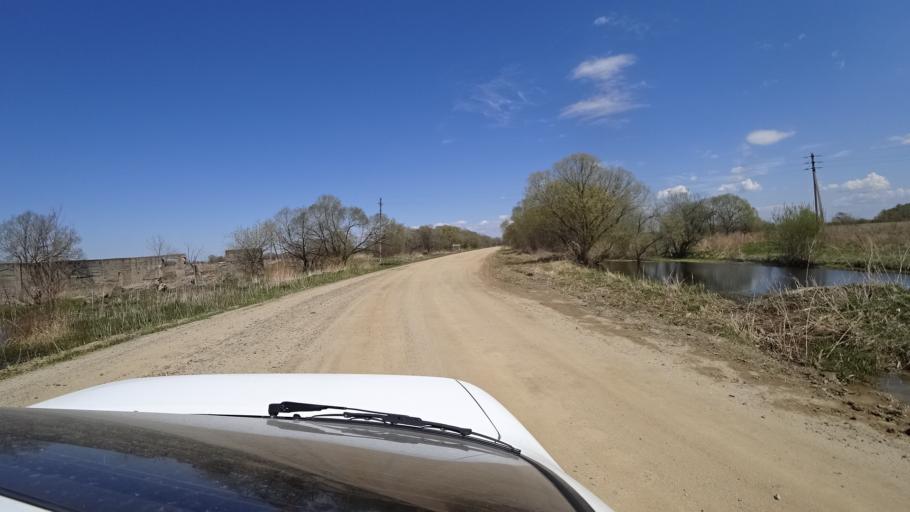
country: RU
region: Primorskiy
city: Dal'nerechensk
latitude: 45.8010
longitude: 133.7725
